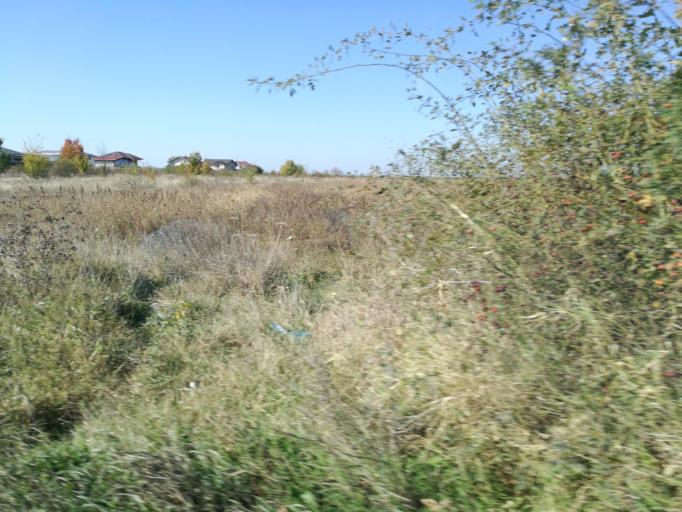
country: RO
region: Giurgiu
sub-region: Comuna Joita
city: Bacu
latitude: 44.4708
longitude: 25.8861
